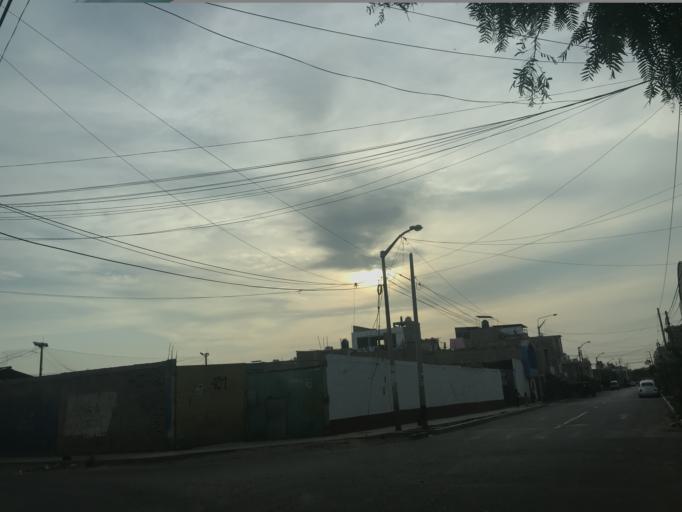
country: PE
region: Lambayeque
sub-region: Provincia de Chiclayo
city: Chiclayo
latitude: -6.7913
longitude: -79.8441
